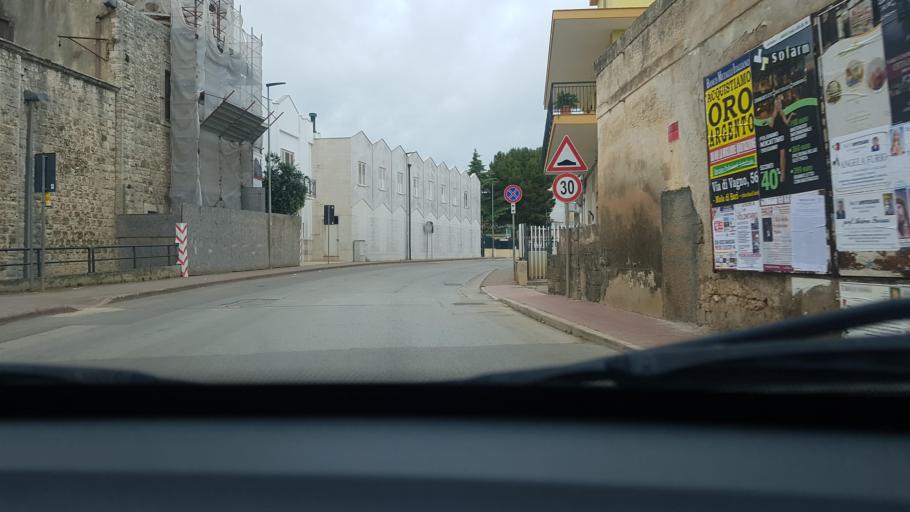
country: IT
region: Apulia
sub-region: Provincia di Bari
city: Noicattaro
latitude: 41.0322
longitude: 16.9822
